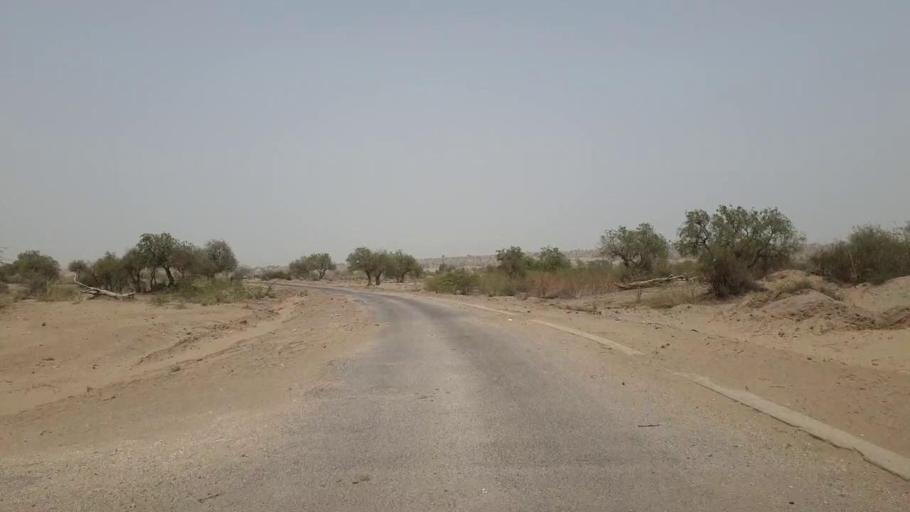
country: PK
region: Sindh
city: Islamkot
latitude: 24.7963
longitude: 70.5422
